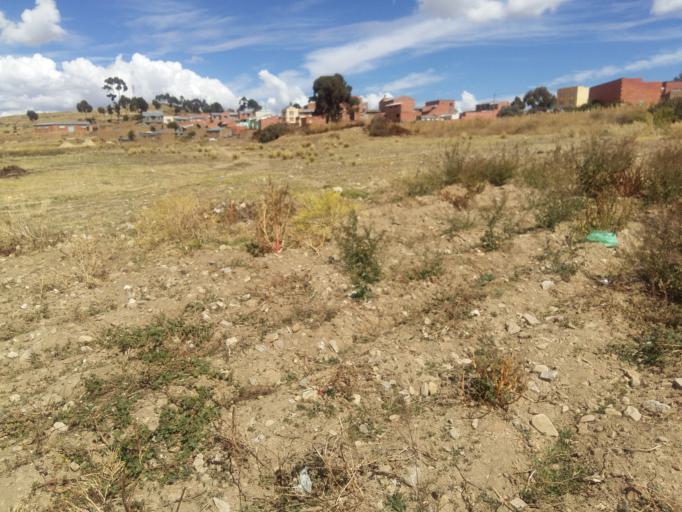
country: BO
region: La Paz
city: Batallas
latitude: -16.2822
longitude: -68.5991
